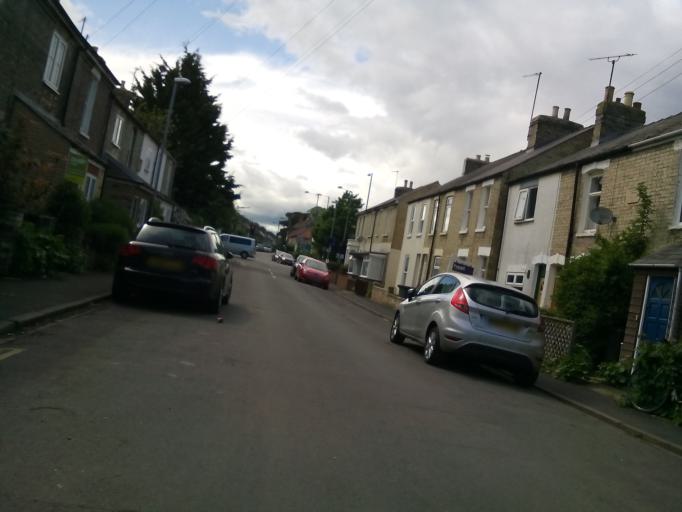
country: GB
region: England
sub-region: Cambridgeshire
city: Cambridge
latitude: 52.1957
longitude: 0.1569
